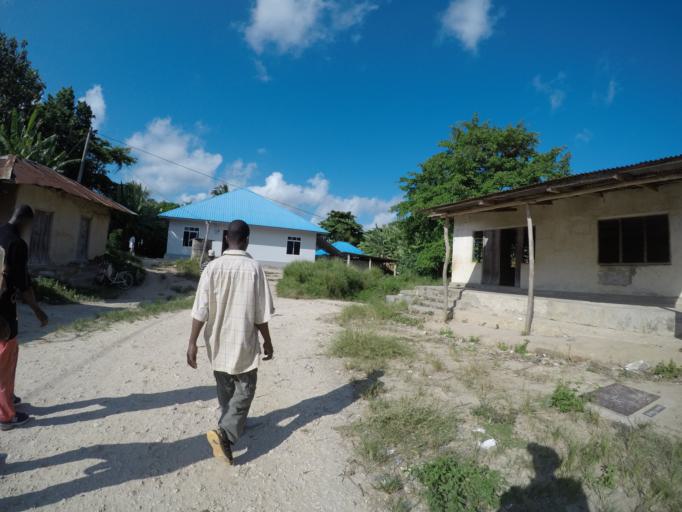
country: TZ
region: Pemba South
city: Mtambile
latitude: -5.3963
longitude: 39.7386
